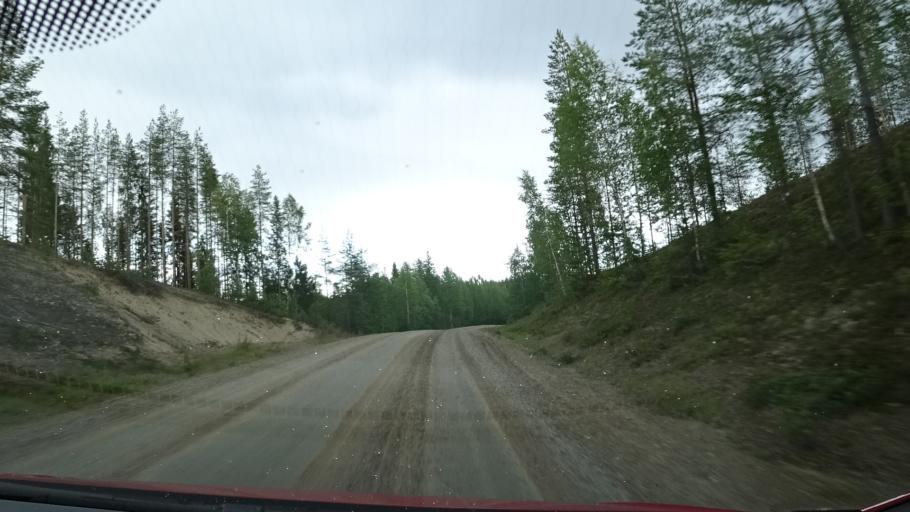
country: FI
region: Kainuu
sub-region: Kehys-Kainuu
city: Kuhmo
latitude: 63.9522
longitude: 29.2220
